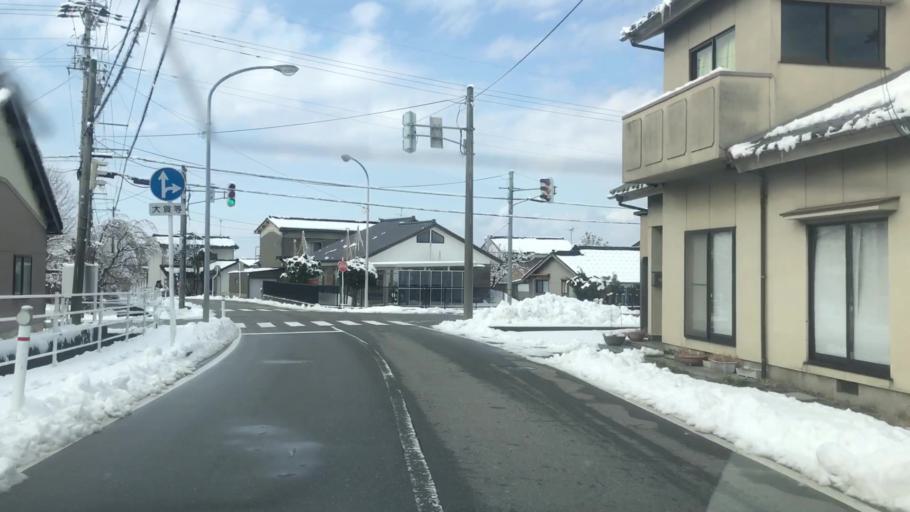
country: JP
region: Toyama
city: Toyama-shi
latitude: 36.6162
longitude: 137.2758
